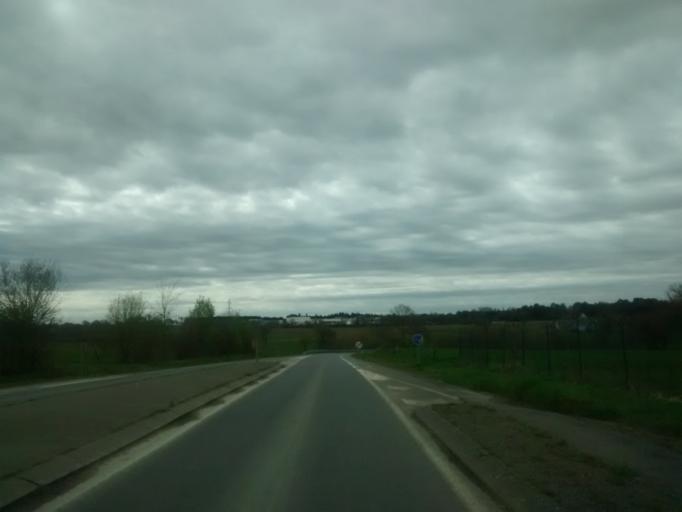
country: FR
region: Brittany
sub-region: Departement d'Ille-et-Vilaine
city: Erce-pres-Liffre
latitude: 48.2427
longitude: -1.5100
